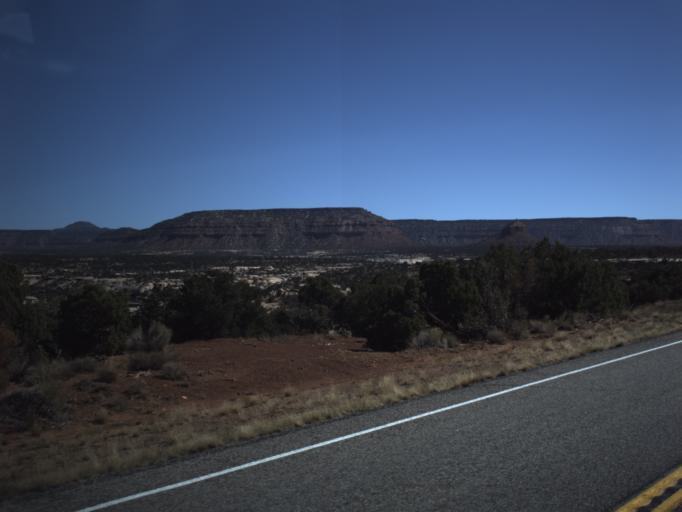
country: US
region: Utah
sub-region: San Juan County
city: Blanding
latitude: 37.6542
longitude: -110.1332
